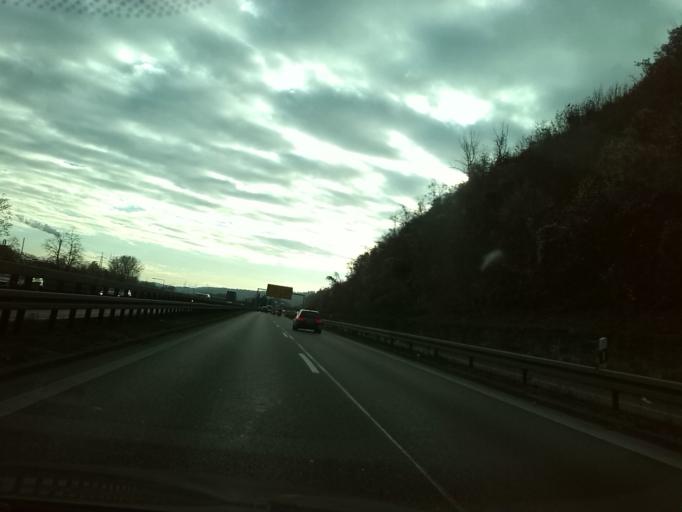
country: DE
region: Baden-Wuerttemberg
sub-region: Regierungsbezirk Stuttgart
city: Esslingen
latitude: 48.7316
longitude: 9.3120
